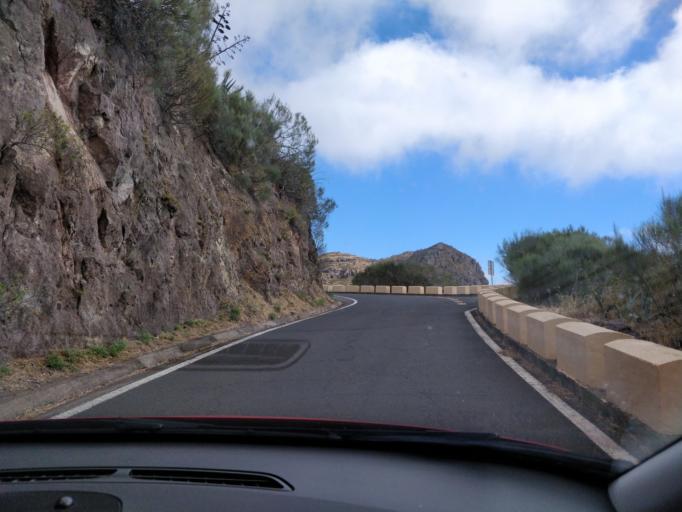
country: ES
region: Canary Islands
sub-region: Provincia de Santa Cruz de Tenerife
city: Santiago del Teide
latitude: 28.3167
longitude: -16.8497
